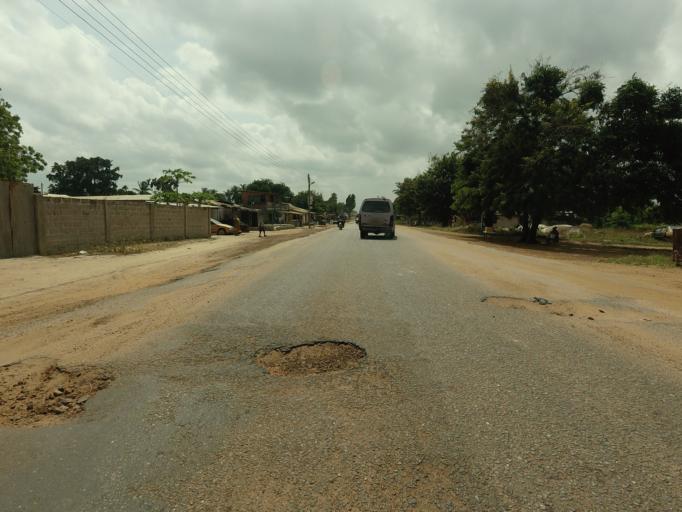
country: TG
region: Maritime
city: Lome
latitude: 6.1214
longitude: 1.1296
